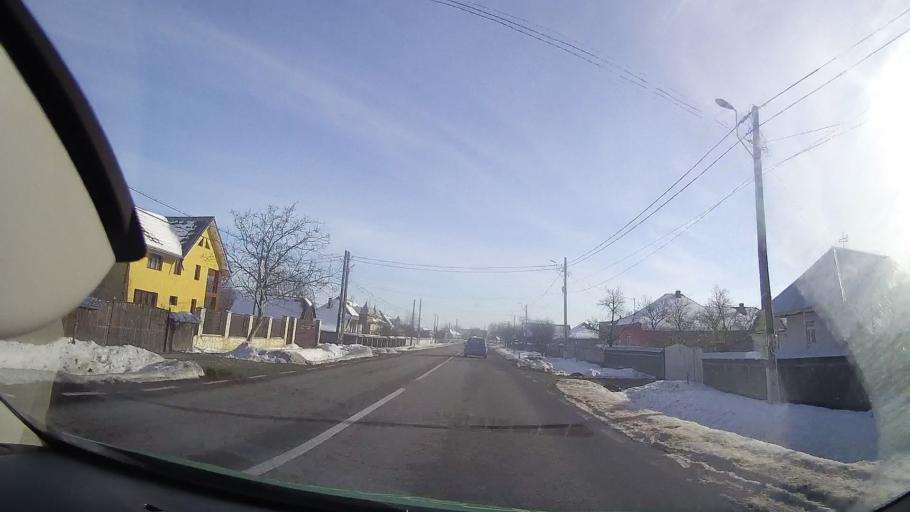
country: RO
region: Neamt
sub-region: Comuna Cracaoani
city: Cracaoani
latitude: 47.0928
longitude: 26.3203
